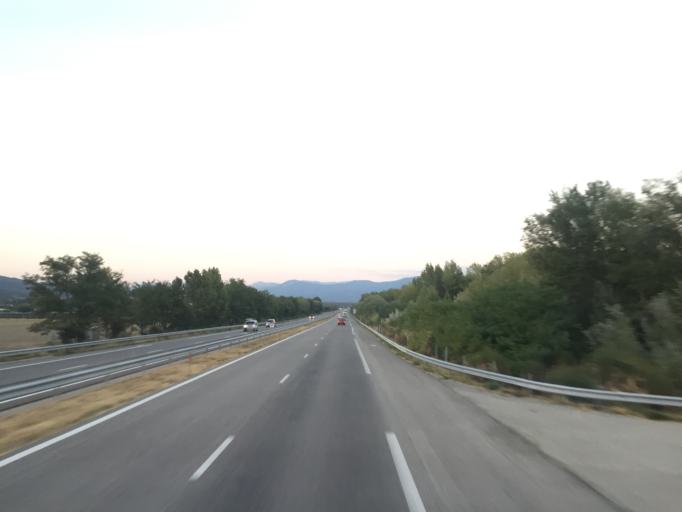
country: FR
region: Provence-Alpes-Cote d'Azur
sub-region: Departement des Alpes-de-Haute-Provence
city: Peyruis
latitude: 44.0189
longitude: 5.9444
